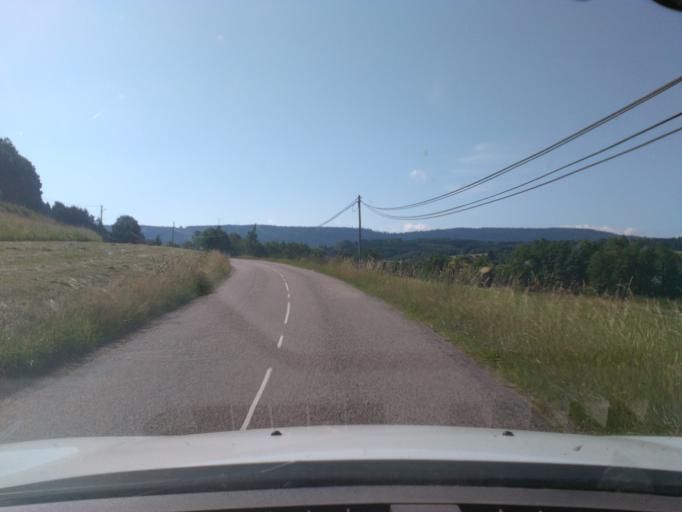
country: FR
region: Lorraine
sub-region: Departement des Vosges
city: Bruyeres
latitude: 48.2401
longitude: 6.7443
